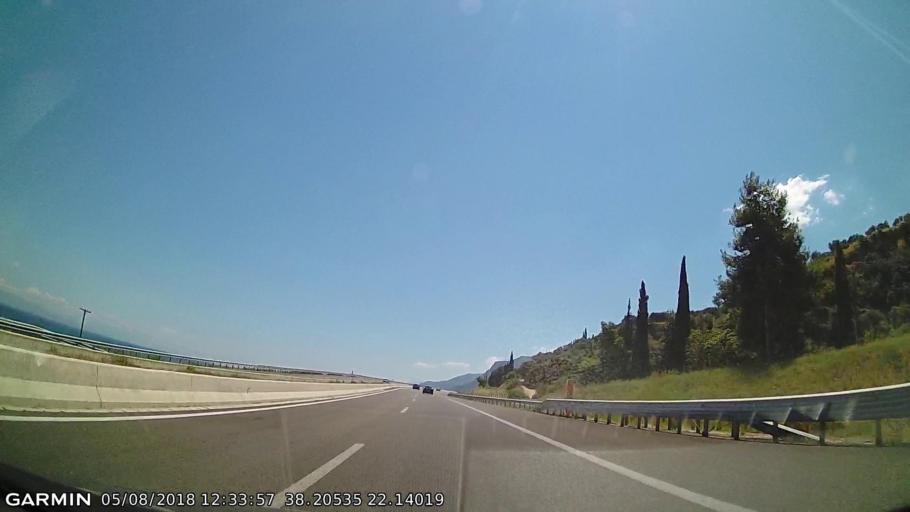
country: GR
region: West Greece
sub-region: Nomos Achaias
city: Temeni
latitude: 38.2049
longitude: 22.1405
